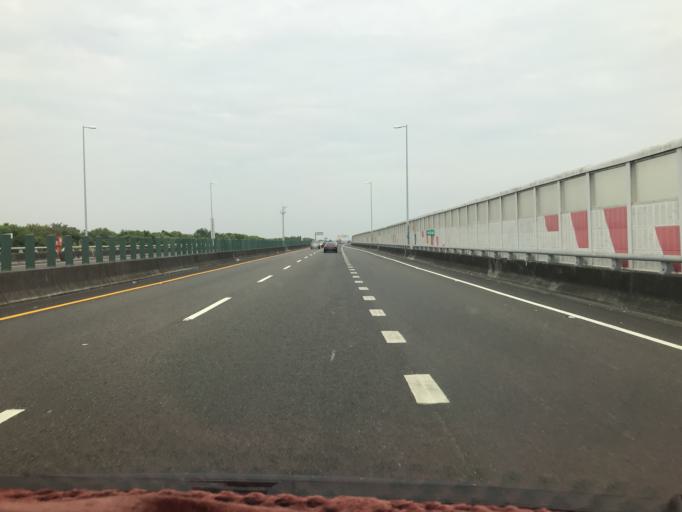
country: TW
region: Taiwan
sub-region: Pingtung
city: Pingtung
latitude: 22.6498
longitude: 120.5451
